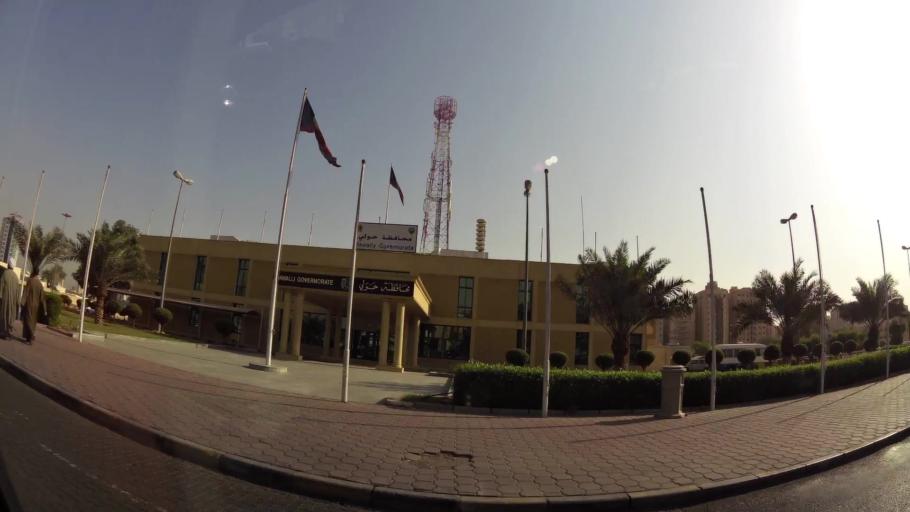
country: KW
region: Muhafazat Hawalli
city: Hawalli
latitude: 29.3374
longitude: 48.0240
